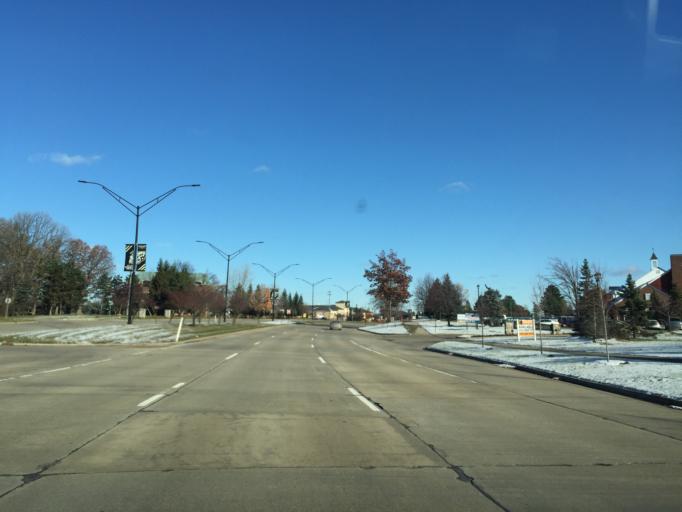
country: US
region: Michigan
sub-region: Oakland County
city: Auburn Hills
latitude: 42.6715
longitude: -83.2285
